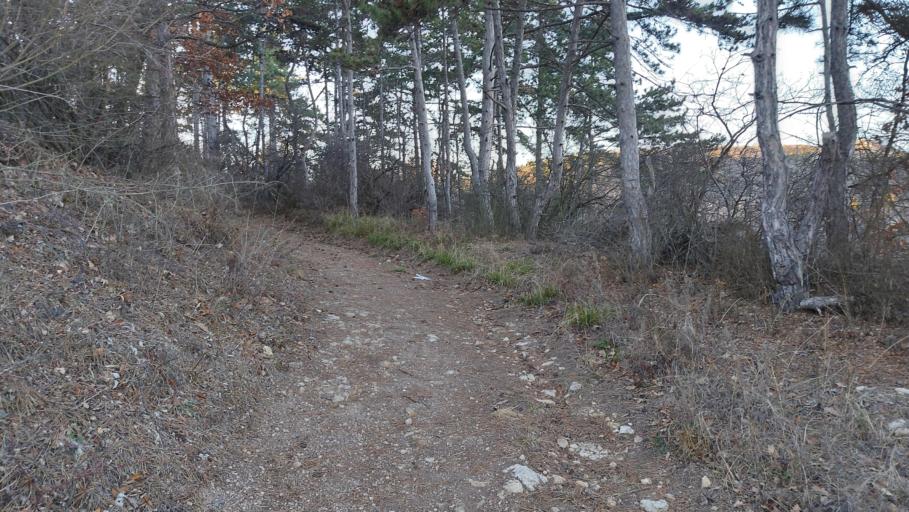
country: HU
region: Pest
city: Budaors
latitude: 47.4658
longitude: 18.9356
